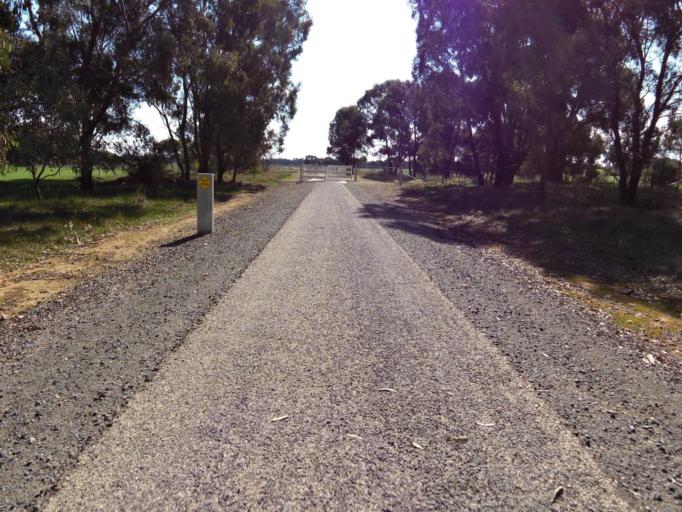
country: AU
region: New South Wales
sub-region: Corowa Shire
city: Corowa
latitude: -36.0372
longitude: 146.4515
